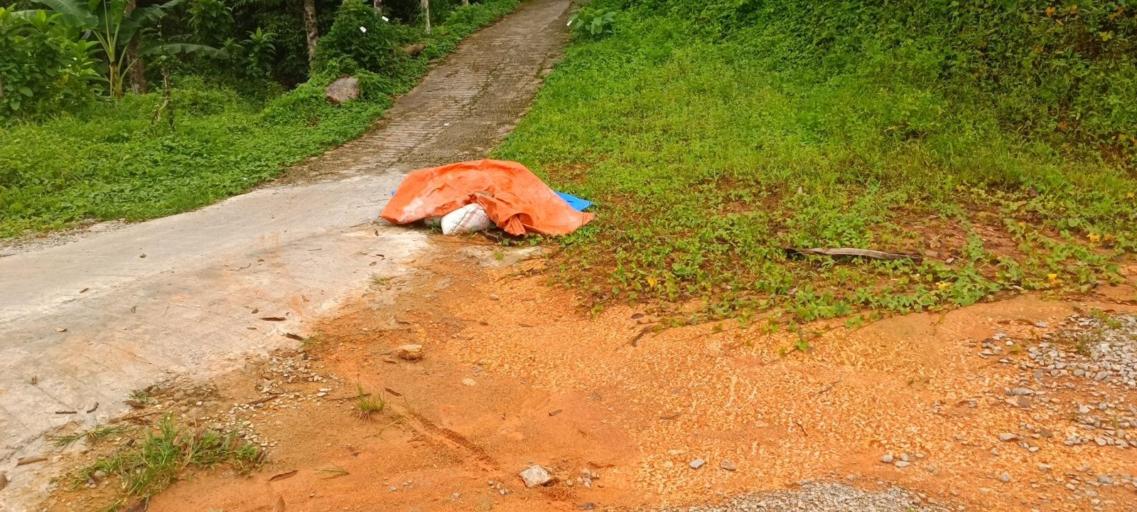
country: MY
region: Penang
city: Bukit Mertajam
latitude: 5.3734
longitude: 100.4765
